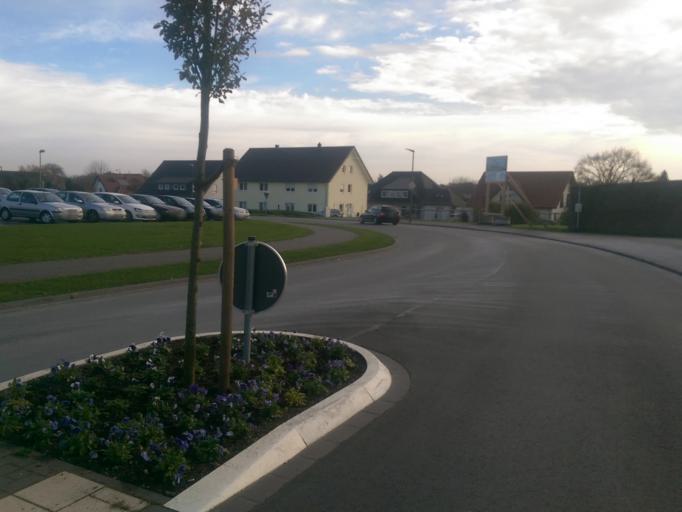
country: DE
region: North Rhine-Westphalia
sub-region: Regierungsbezirk Detmold
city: Delbruck
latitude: 51.7626
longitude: 8.5589
